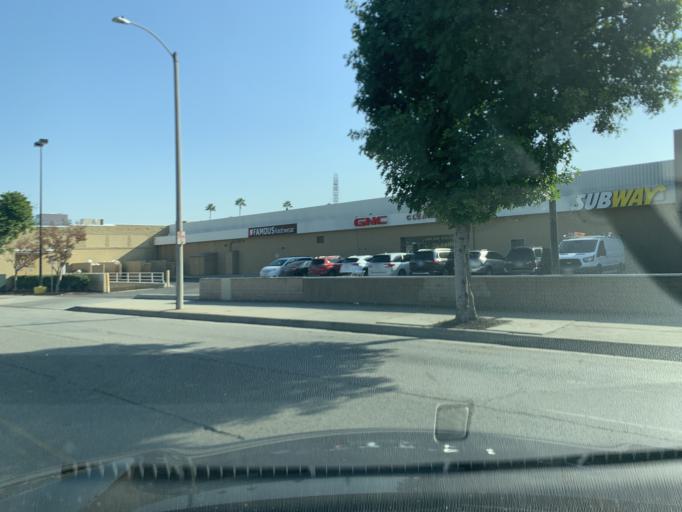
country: US
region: California
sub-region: Los Angeles County
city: Covina
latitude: 34.0754
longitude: -117.8884
